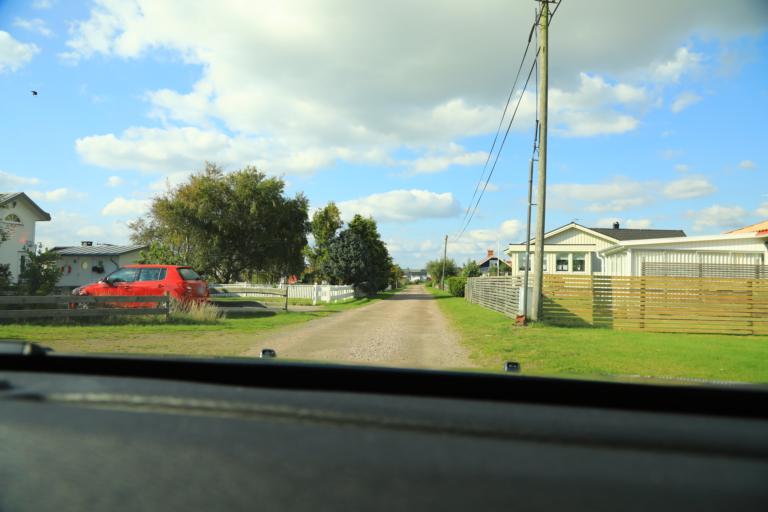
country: SE
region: Halland
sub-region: Varbergs Kommun
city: Tvaaker
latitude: 57.0137
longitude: 12.3479
